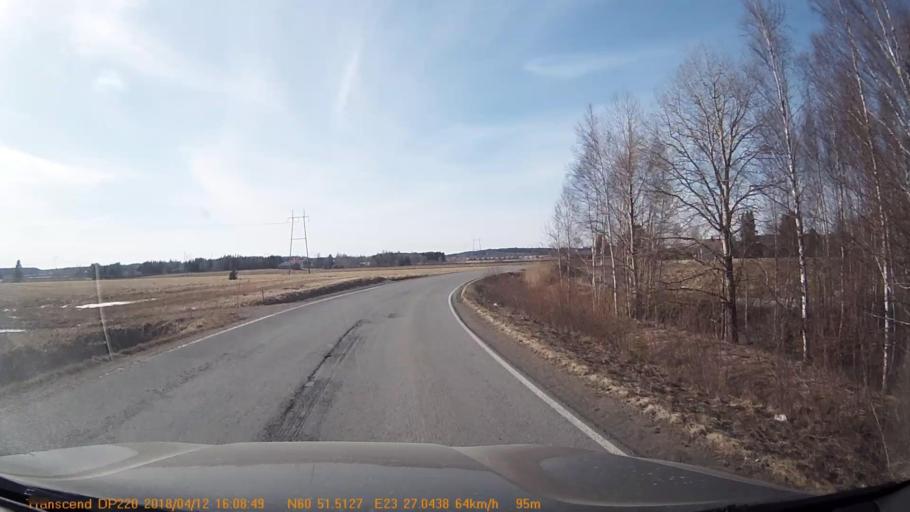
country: FI
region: Haeme
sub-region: Forssa
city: Jokioinen
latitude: 60.8581
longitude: 23.4515
